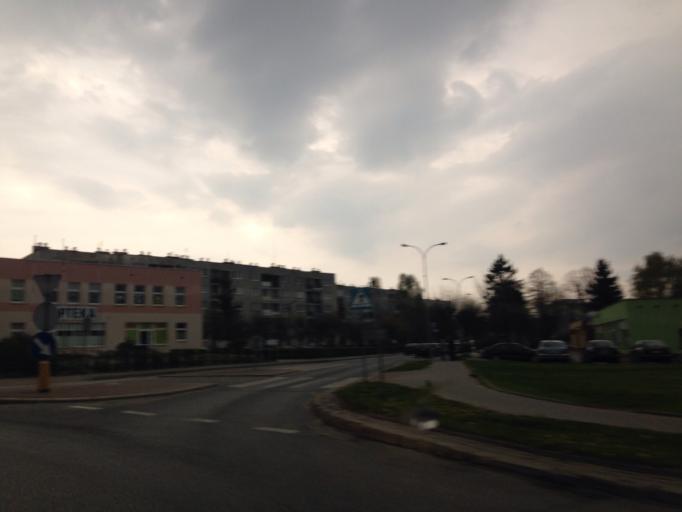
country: PL
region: Masovian Voivodeship
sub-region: Powiat plonski
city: Plonsk
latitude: 52.6316
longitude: 20.3673
